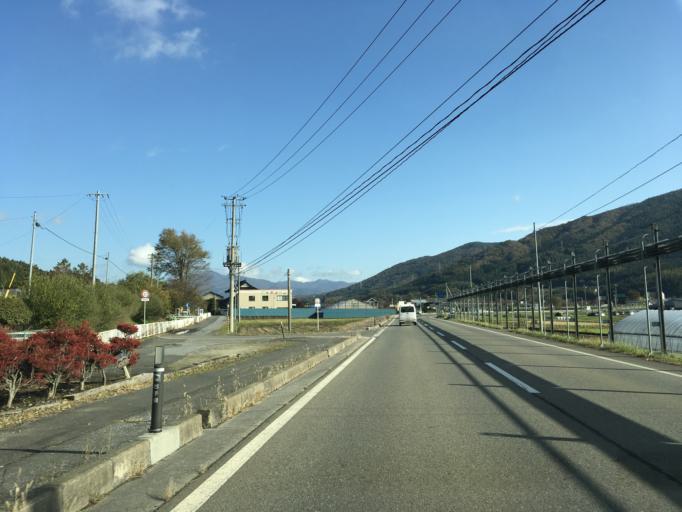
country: JP
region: Iwate
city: Tono
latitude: 39.3315
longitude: 141.4787
